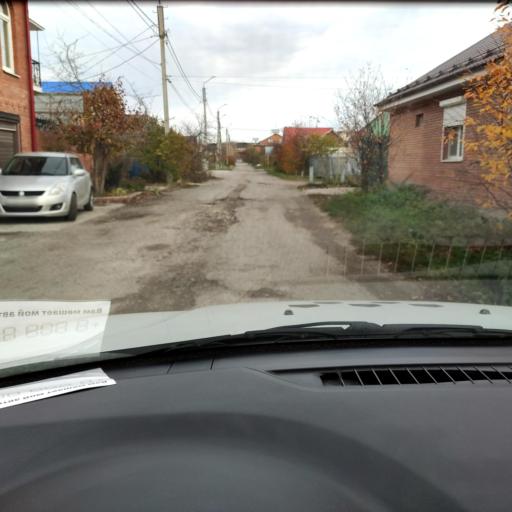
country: RU
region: Samara
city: Tol'yatti
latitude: 53.5107
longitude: 49.3986
